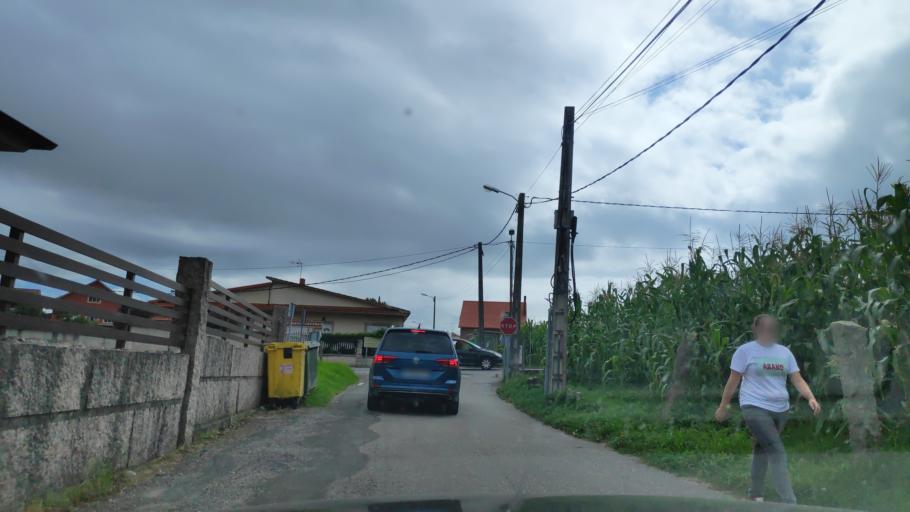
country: ES
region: Galicia
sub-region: Provincia da Coruna
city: Rianxo
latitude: 42.6706
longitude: -8.8156
